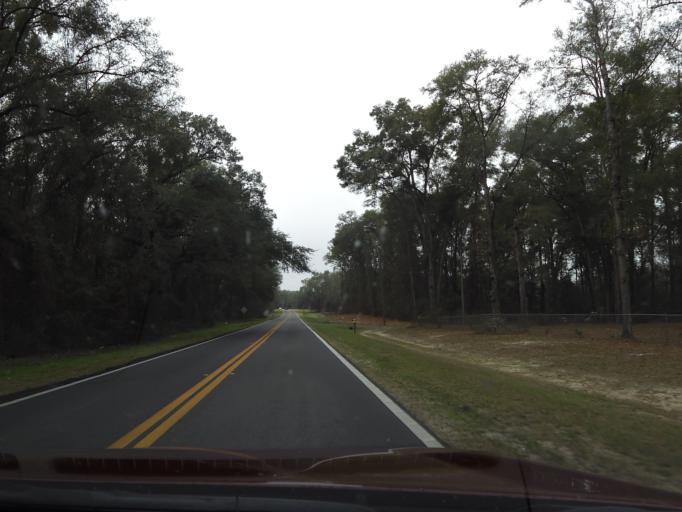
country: US
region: Florida
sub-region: Alachua County
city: High Springs
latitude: 29.8523
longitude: -82.5781
